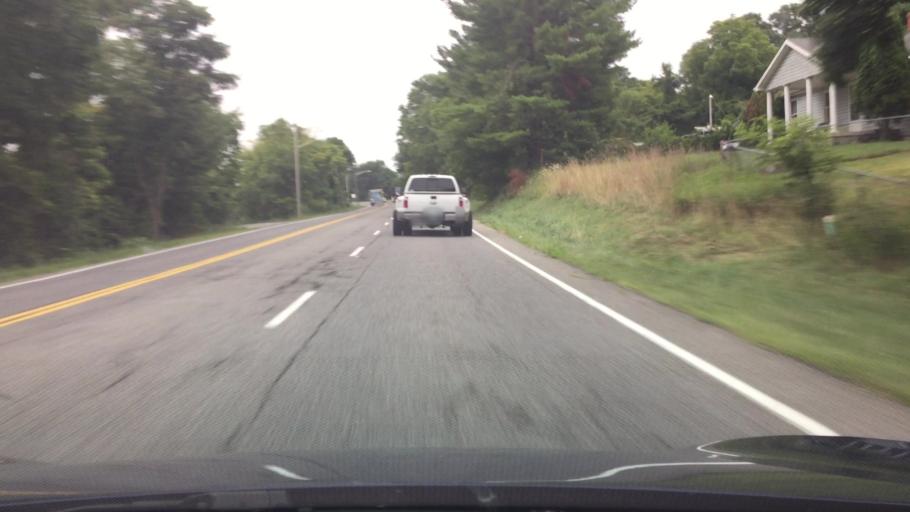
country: US
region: Virginia
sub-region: Montgomery County
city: Christiansburg
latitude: 37.1393
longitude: -80.3343
